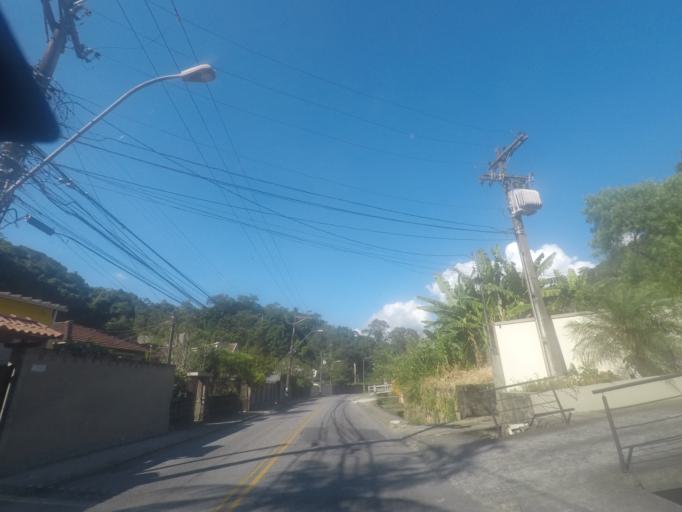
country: BR
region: Rio de Janeiro
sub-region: Petropolis
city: Petropolis
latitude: -22.5285
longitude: -43.1902
